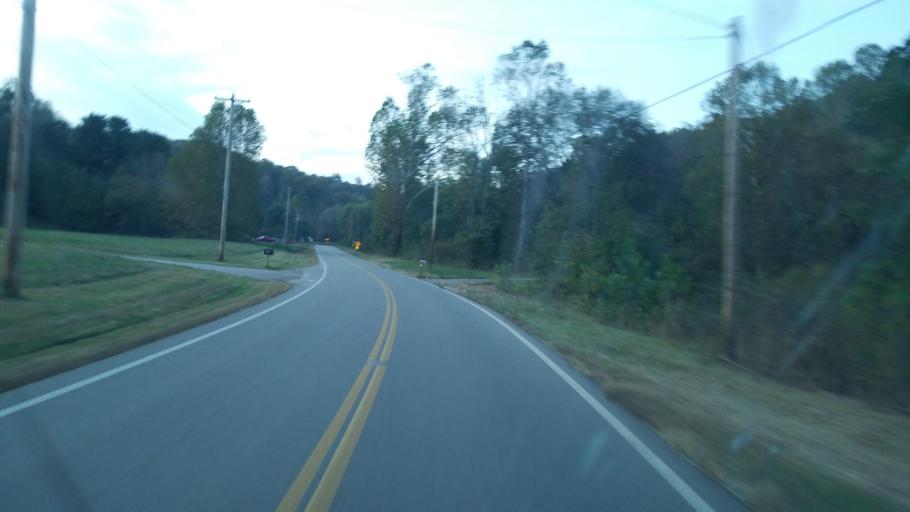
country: US
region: Ohio
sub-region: Meigs County
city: Pomeroy
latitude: 39.0433
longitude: -82.0630
